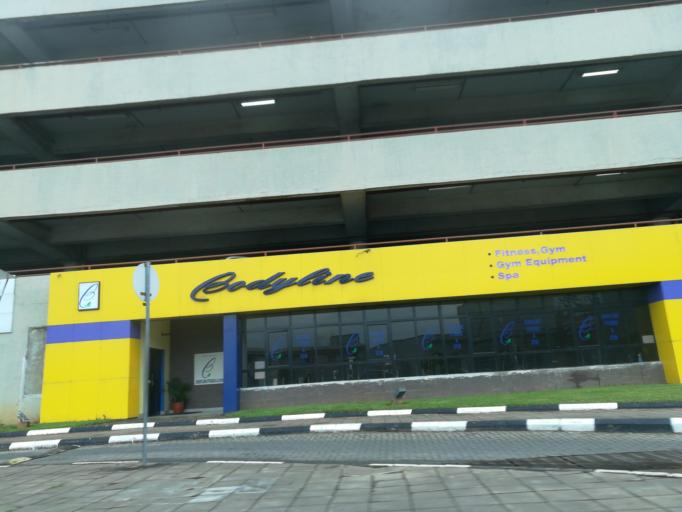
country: NG
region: Lagos
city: Ikeja
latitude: 6.5856
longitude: 3.3333
